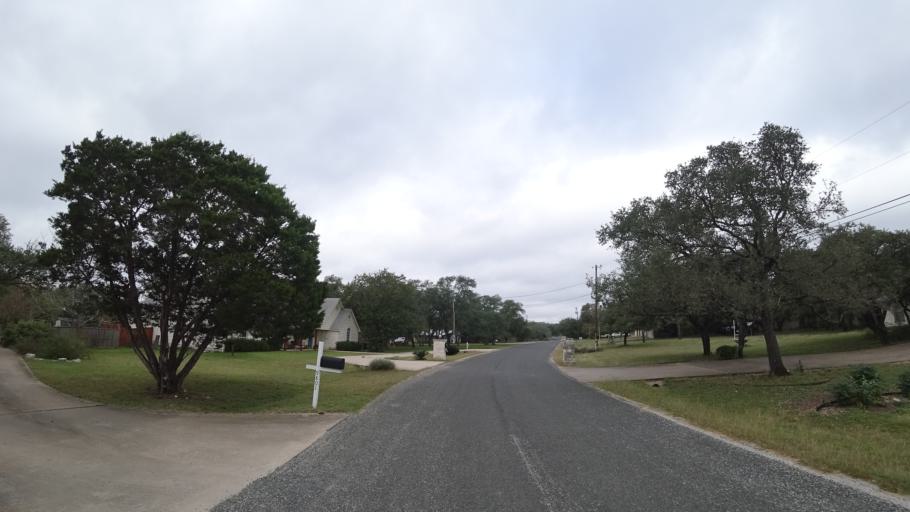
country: US
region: Texas
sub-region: Travis County
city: Barton Creek
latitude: 30.2498
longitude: -97.9148
